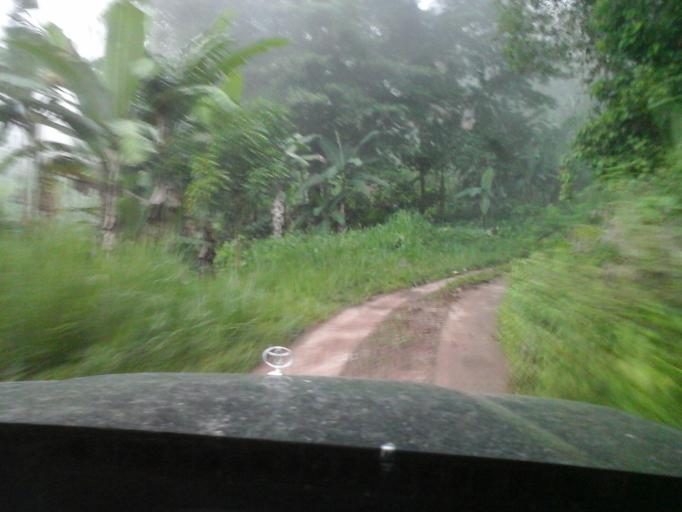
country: CO
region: Cesar
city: Agustin Codazzi
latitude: 9.9424
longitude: -73.1244
